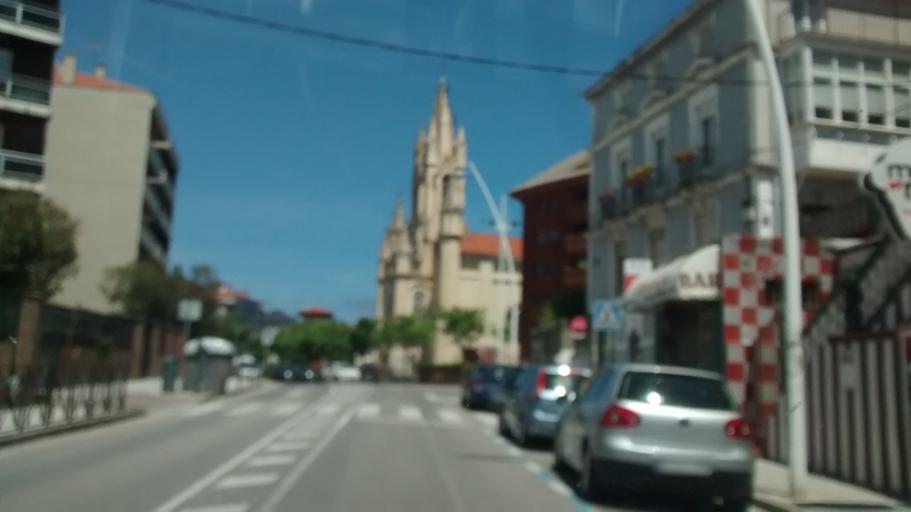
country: ES
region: Cantabria
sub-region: Provincia de Cantabria
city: Santander
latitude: 43.4666
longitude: -3.7871
